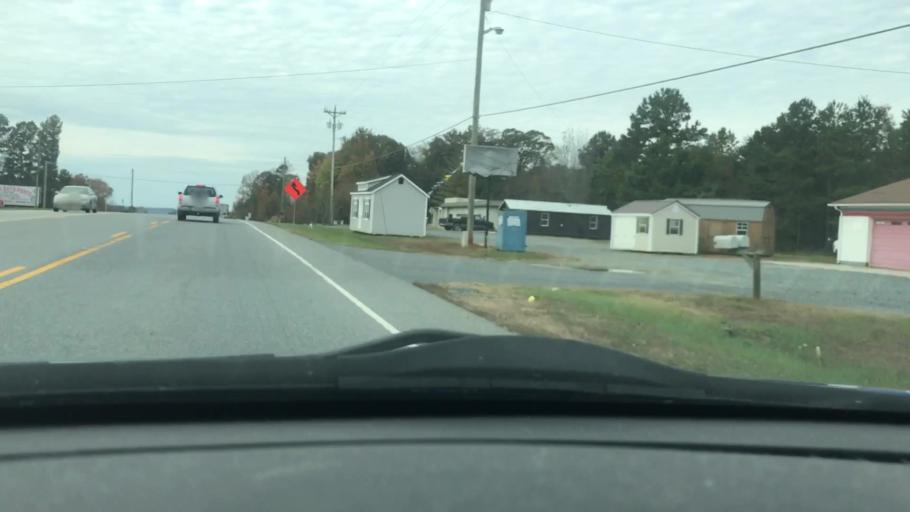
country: US
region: North Carolina
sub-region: Randolph County
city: Asheboro
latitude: 35.6923
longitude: -79.8524
